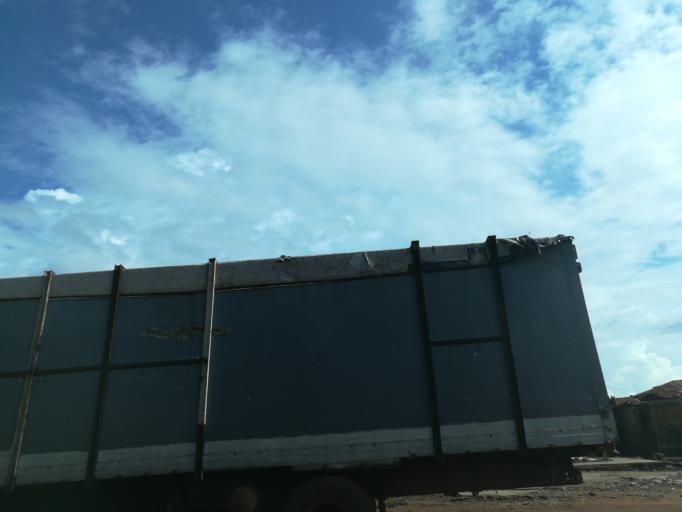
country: NG
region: Lagos
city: Ikorodu
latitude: 6.5921
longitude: 3.5184
